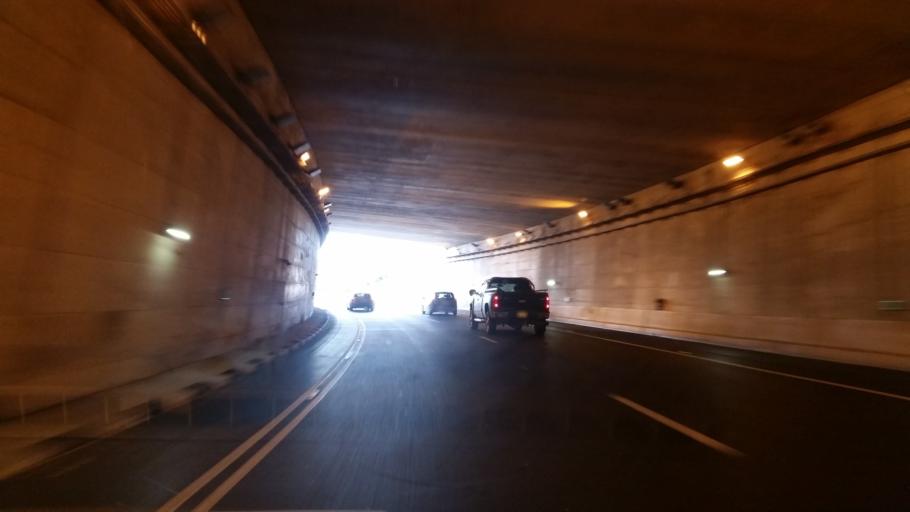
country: IL
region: Tel Aviv
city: Kefar Shemaryahu
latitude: 32.1938
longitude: 34.8302
